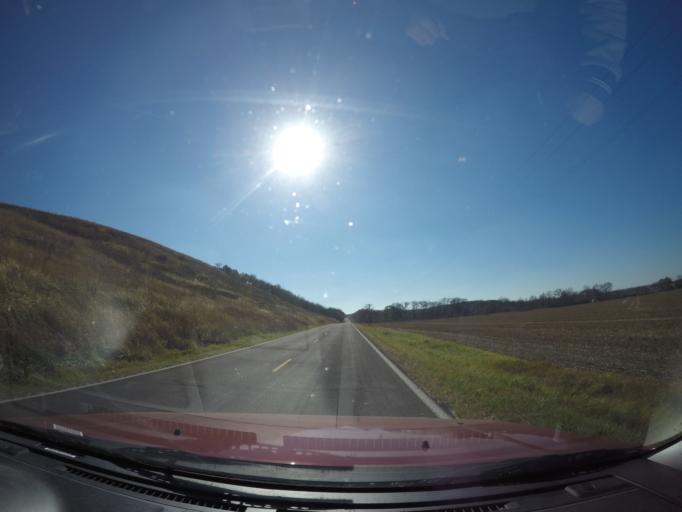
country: US
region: Kansas
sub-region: Geary County
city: Grandview Plaza
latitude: 39.0032
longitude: -96.7306
